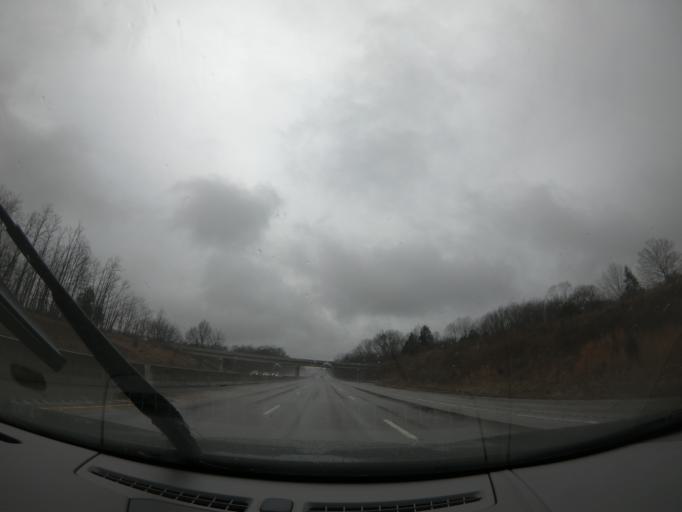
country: US
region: Kentucky
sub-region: Barren County
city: Cave City
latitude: 37.0642
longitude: -86.1010
